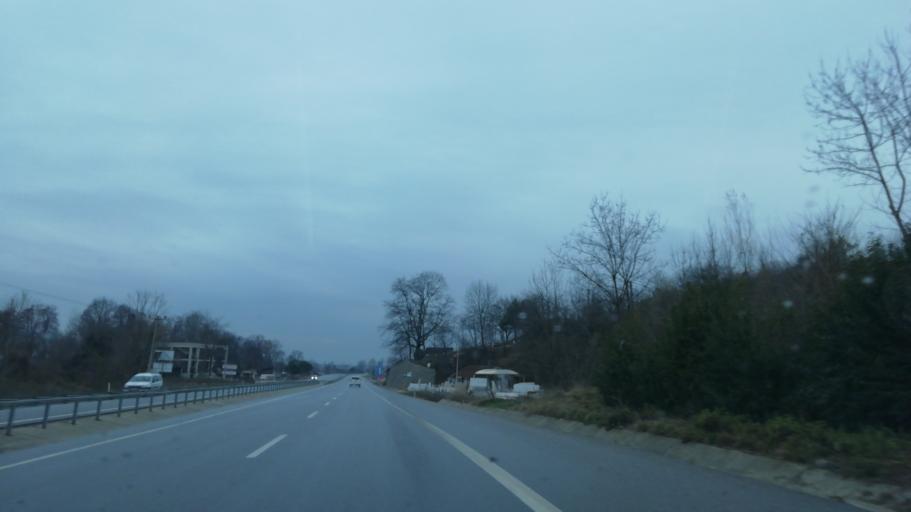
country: TR
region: Sakarya
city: Akyazi
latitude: 40.6305
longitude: 30.6397
